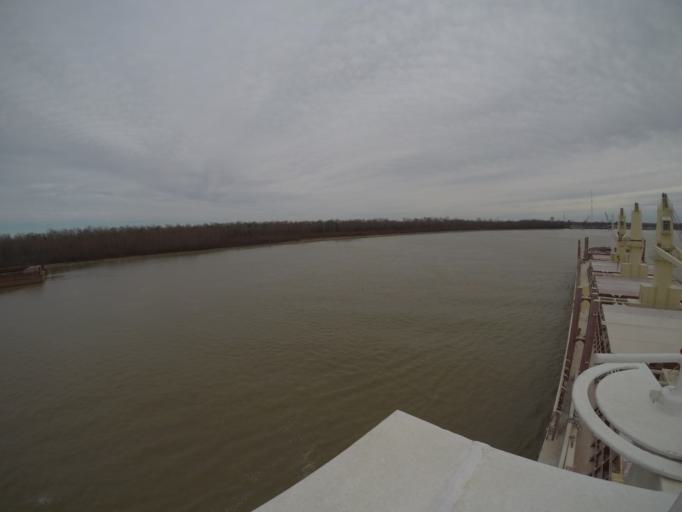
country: US
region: Louisiana
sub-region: Saint John the Baptist Parish
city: Laplace
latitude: 30.0522
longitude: -90.4885
